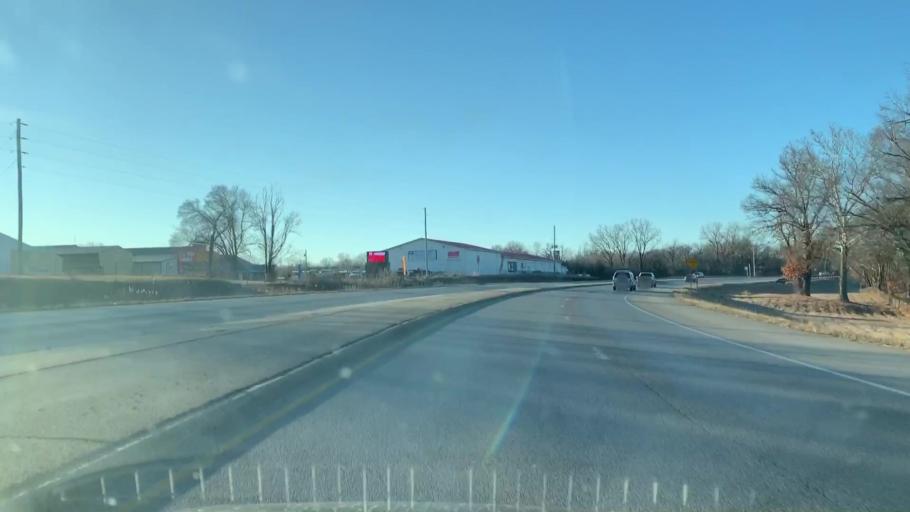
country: US
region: Kansas
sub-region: Bourbon County
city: Fort Scott
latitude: 37.8298
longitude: -94.7019
